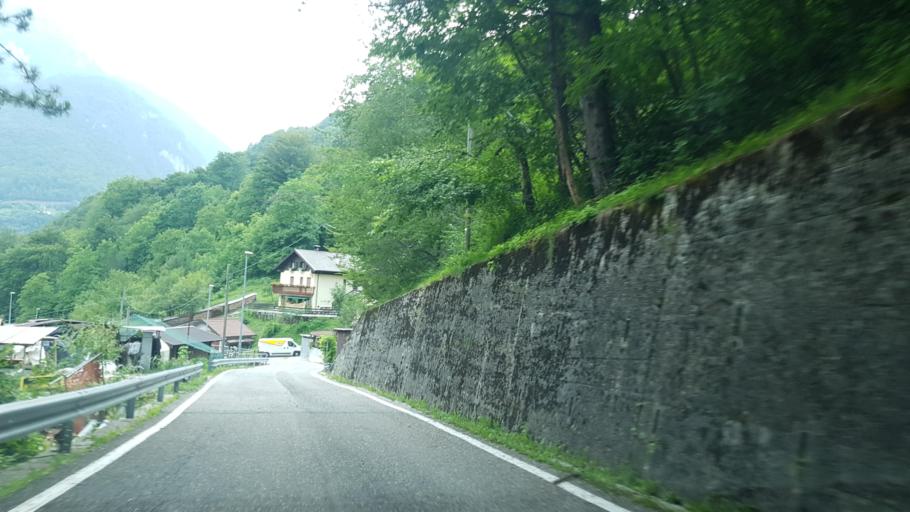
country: IT
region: Friuli Venezia Giulia
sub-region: Provincia di Udine
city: Dogna
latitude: 46.4495
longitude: 13.3328
